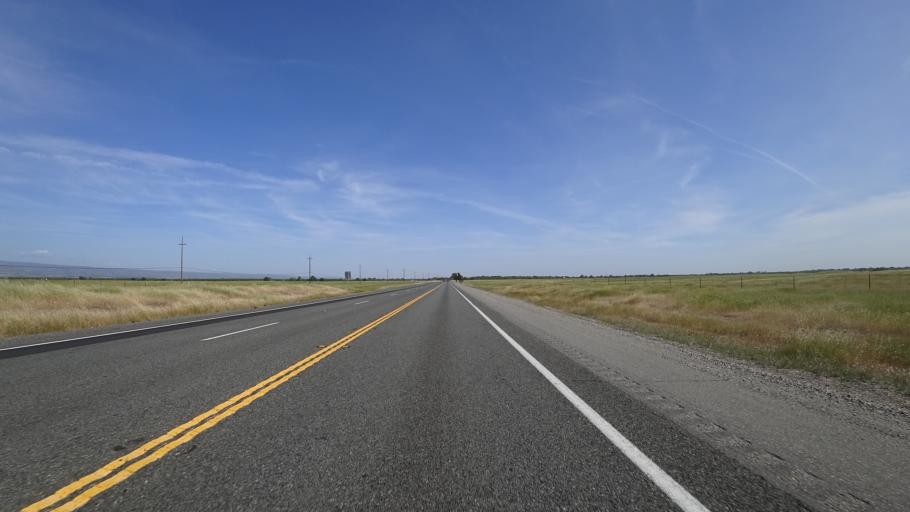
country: US
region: California
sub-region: Glenn County
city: Hamilton City
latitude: 39.8967
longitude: -121.9928
